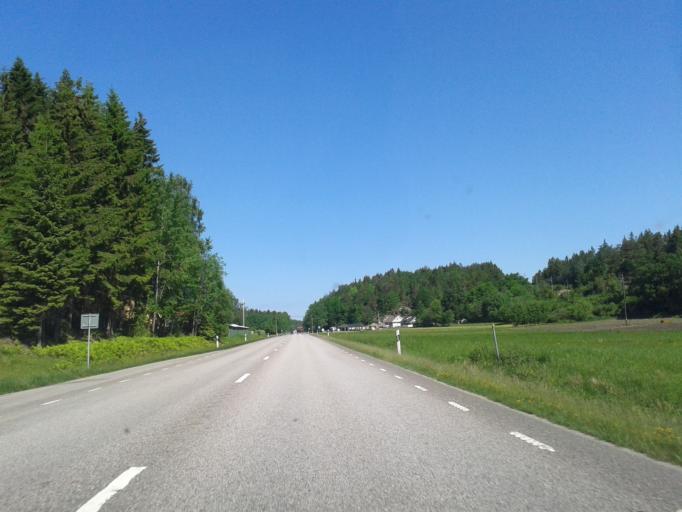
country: SE
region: Vaestra Goetaland
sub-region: Orust
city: Henan
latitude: 58.1795
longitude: 11.6959
